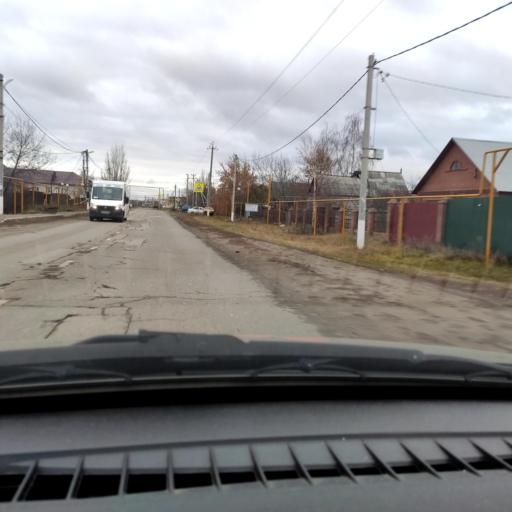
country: RU
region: Samara
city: Podstepki
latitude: 53.5164
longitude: 49.1195
